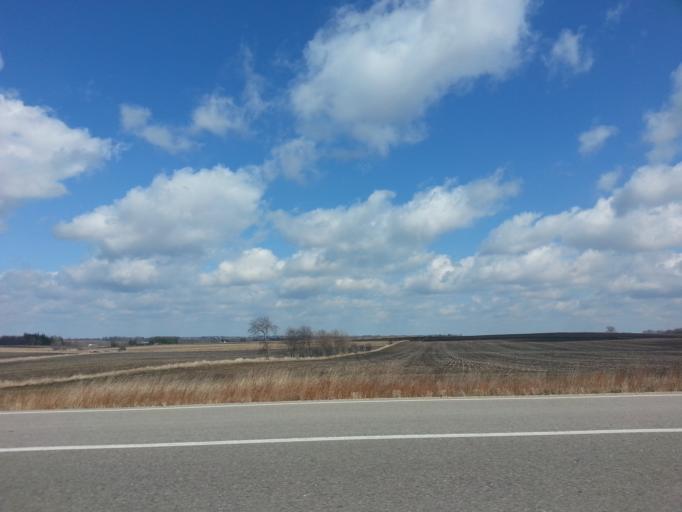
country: US
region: Minnesota
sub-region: Dodge County
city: Dodge Center
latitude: 44.1605
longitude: -92.8996
